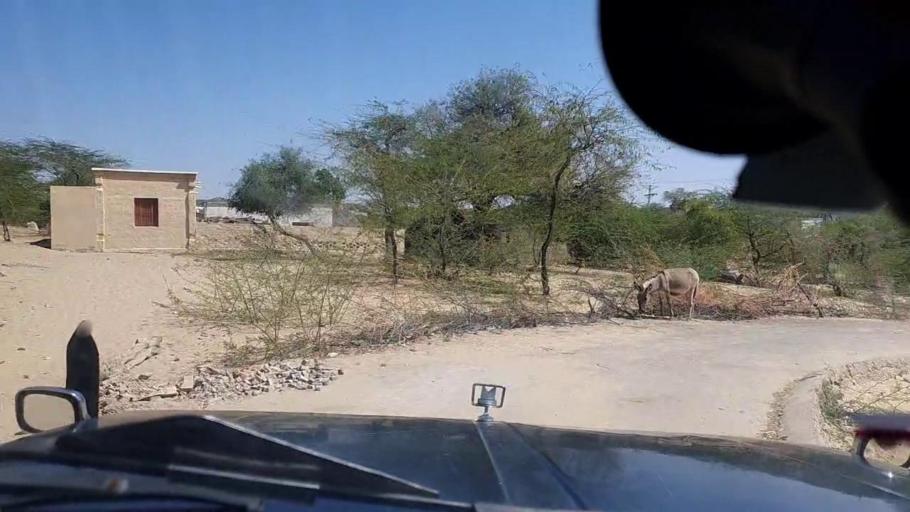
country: PK
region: Sindh
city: Diplo
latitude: 24.5664
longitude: 69.6789
